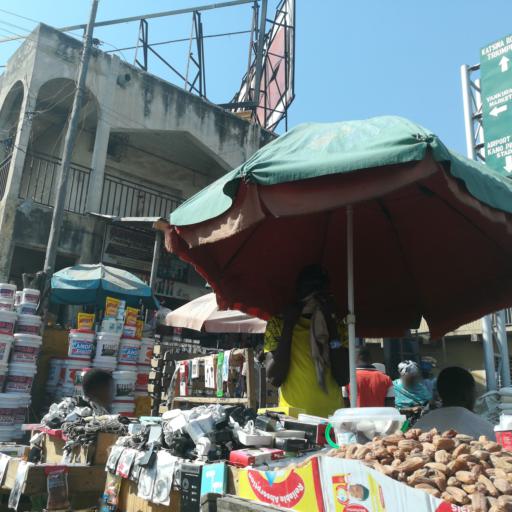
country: NG
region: Kano
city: Kano
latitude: 12.0143
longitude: 8.5353
